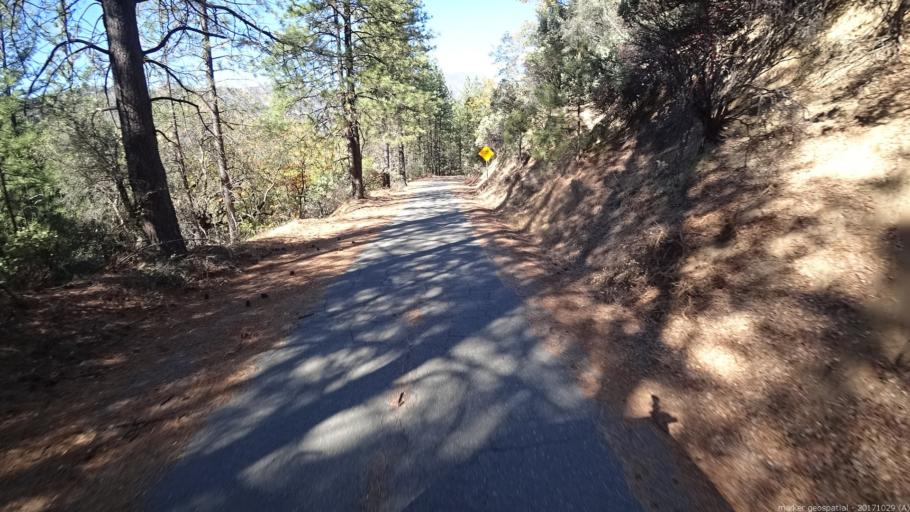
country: US
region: California
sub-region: Shasta County
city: Shasta
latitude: 40.4999
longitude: -122.6900
